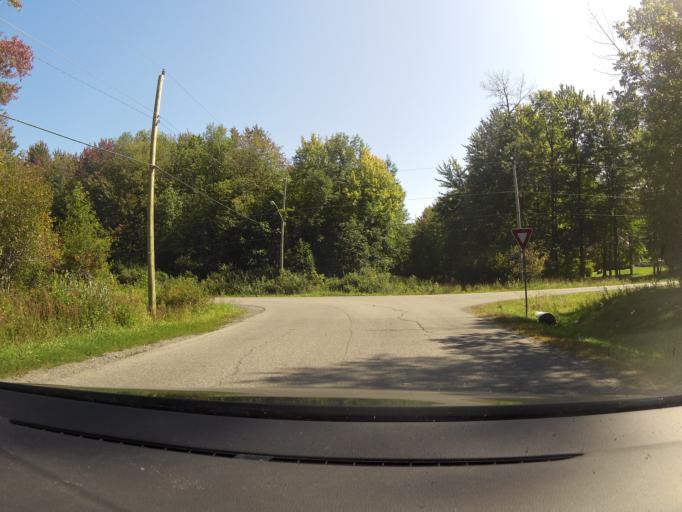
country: CA
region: Ontario
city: Bells Corners
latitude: 45.2873
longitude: -75.9902
